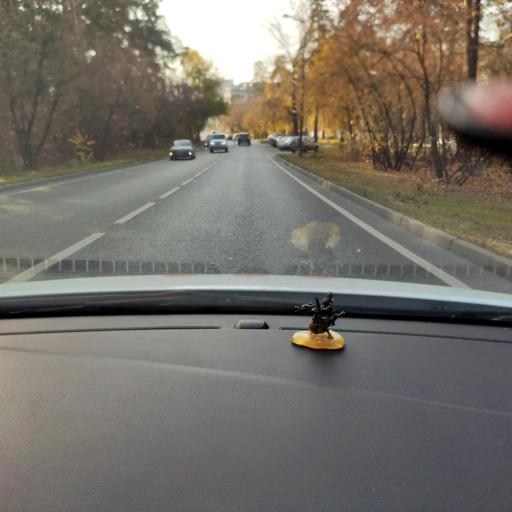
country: RU
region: Tatarstan
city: Osinovo
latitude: 55.8242
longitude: 48.8972
